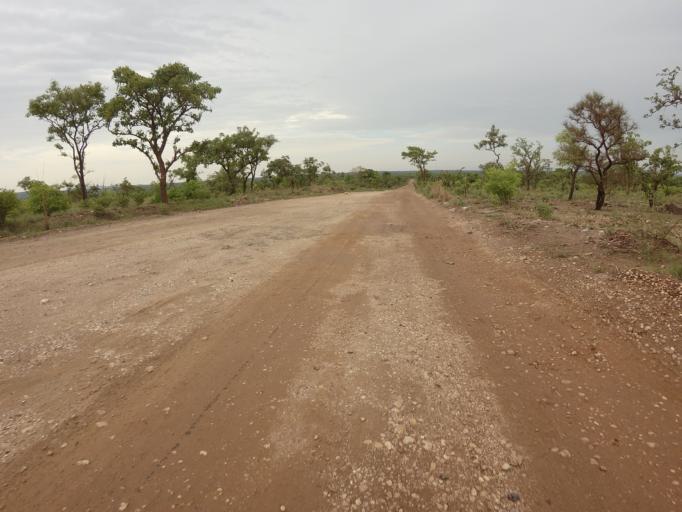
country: GH
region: Upper East
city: Bolgatanga
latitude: 10.8789
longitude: -0.6246
